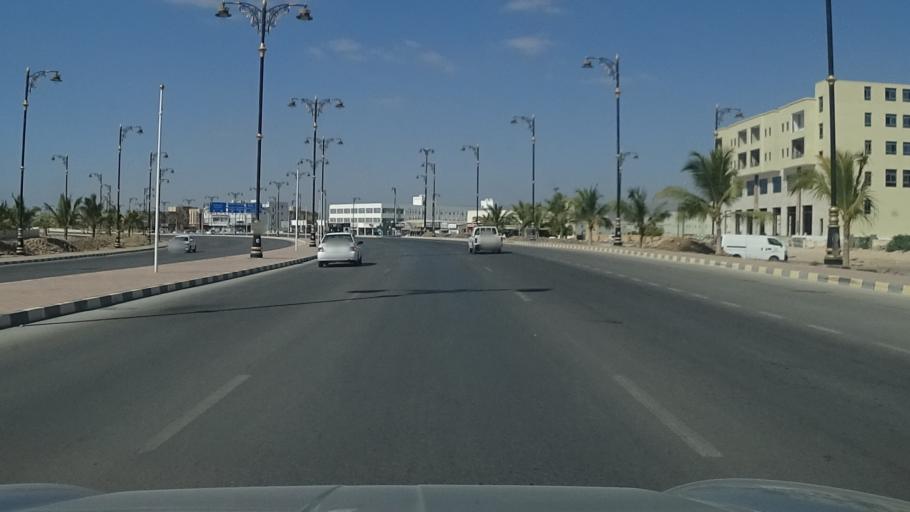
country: OM
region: Zufar
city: Salalah
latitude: 17.0366
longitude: 54.1507
